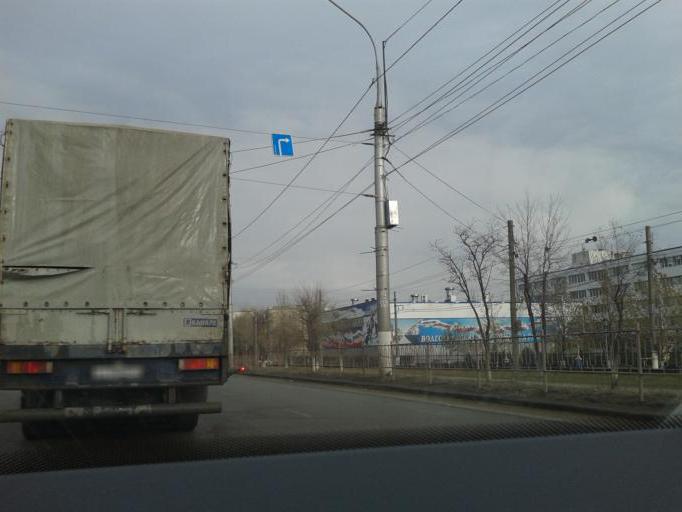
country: RU
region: Volgograd
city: Volgograd
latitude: 48.7554
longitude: 44.4814
